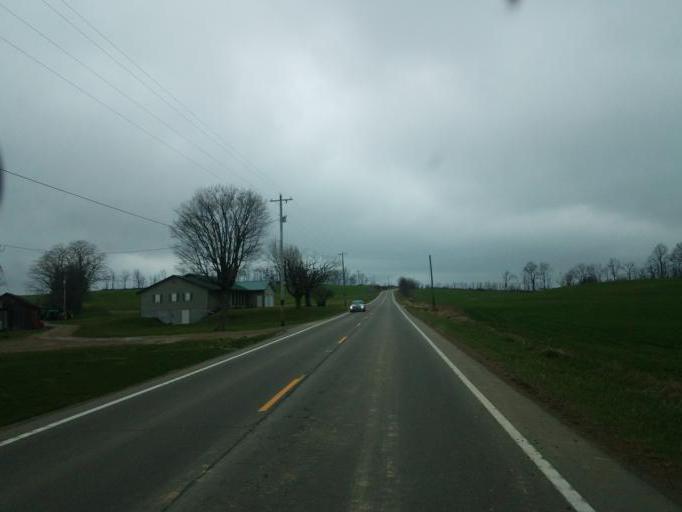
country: US
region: Ohio
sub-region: Ashland County
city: Loudonville
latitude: 40.7447
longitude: -82.2522
